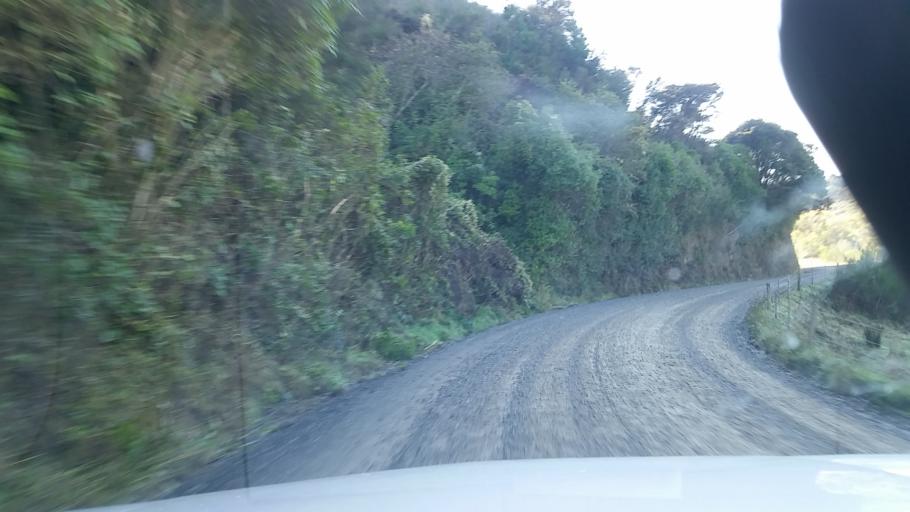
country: NZ
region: Marlborough
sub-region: Marlborough District
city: Blenheim
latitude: -41.4447
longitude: 173.8852
